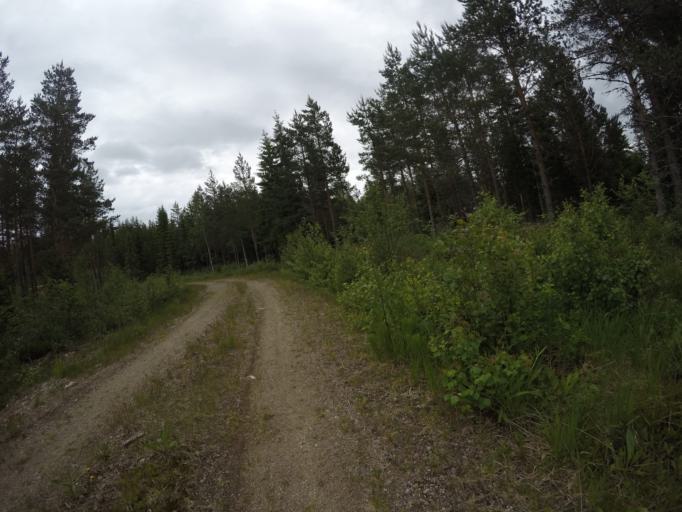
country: SE
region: Dalarna
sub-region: Ludvika Kommun
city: Abborrberget
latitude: 60.0925
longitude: 14.5109
